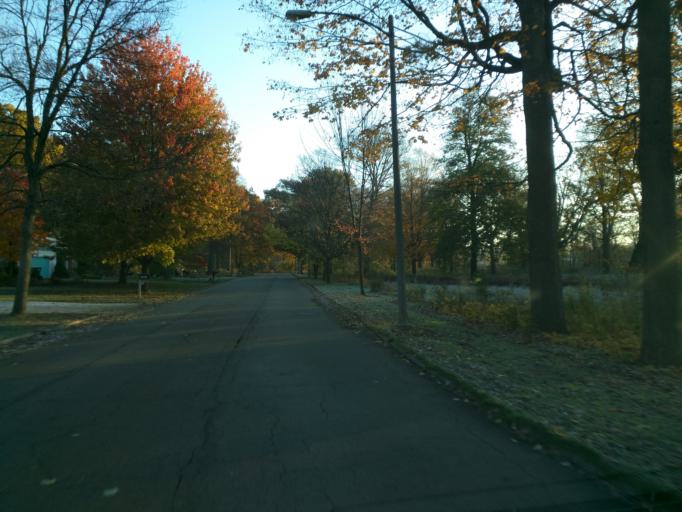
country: US
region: Michigan
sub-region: Ingham County
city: Edgemont Park
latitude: 42.7578
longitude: -84.5812
